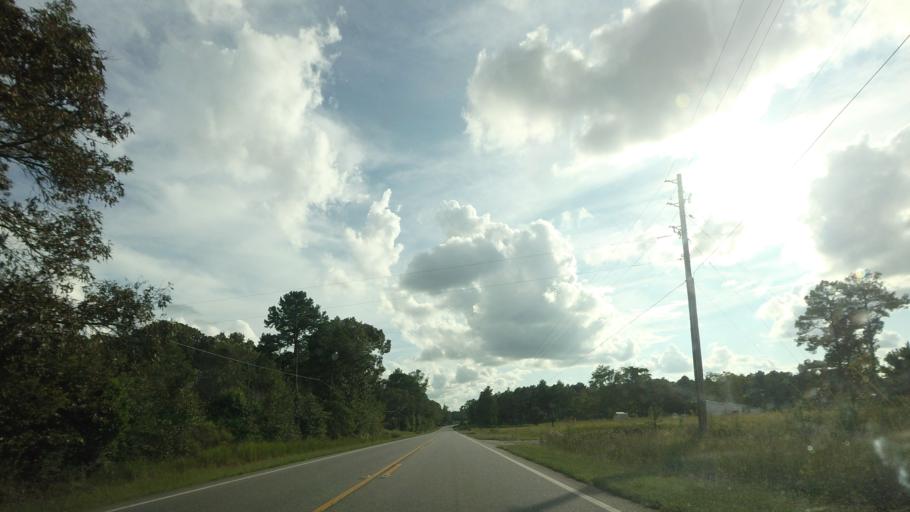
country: US
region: Georgia
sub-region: Pulaski County
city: Hawkinsville
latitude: 32.2981
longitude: -83.4306
